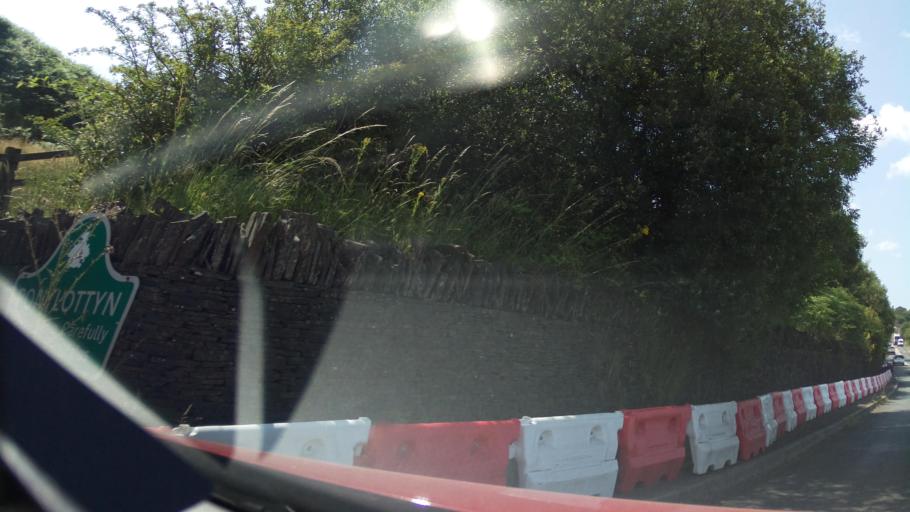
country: GB
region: Wales
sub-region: Caerphilly County Borough
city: Rhymney
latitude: 51.7392
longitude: -3.2730
